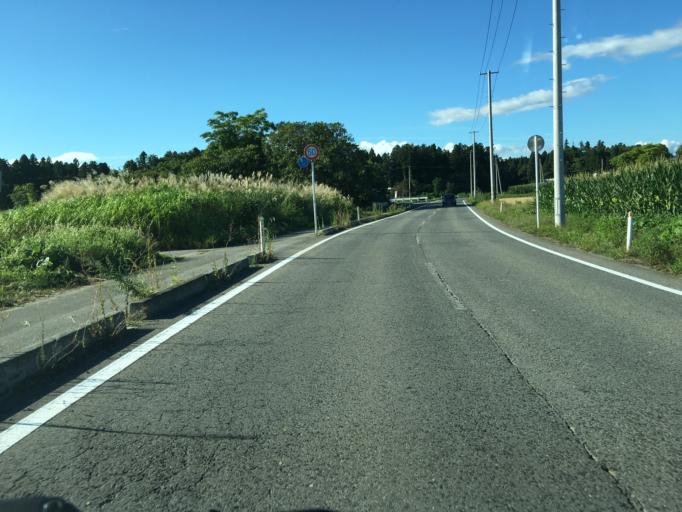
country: JP
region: Yamagata
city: Takahata
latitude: 37.9781
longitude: 140.1559
